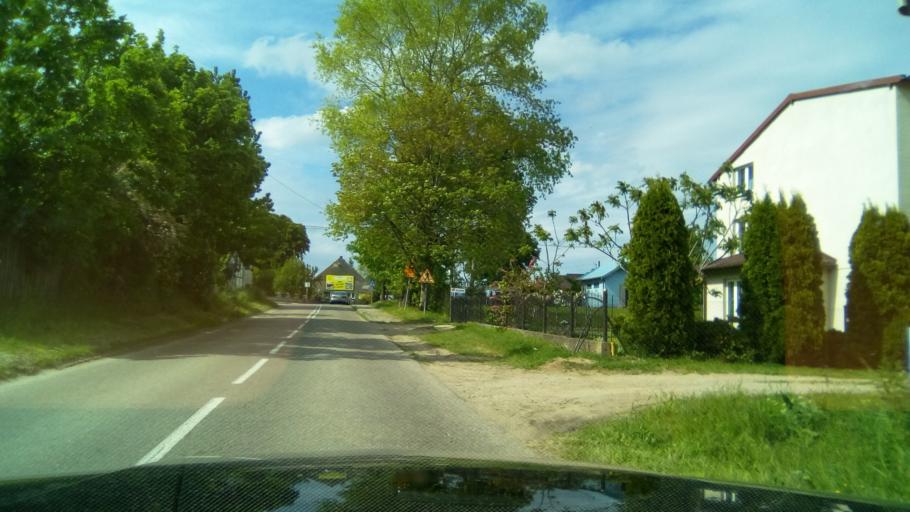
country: PL
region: Pomeranian Voivodeship
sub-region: Powiat pucki
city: Krokowa
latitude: 54.7926
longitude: 18.1170
